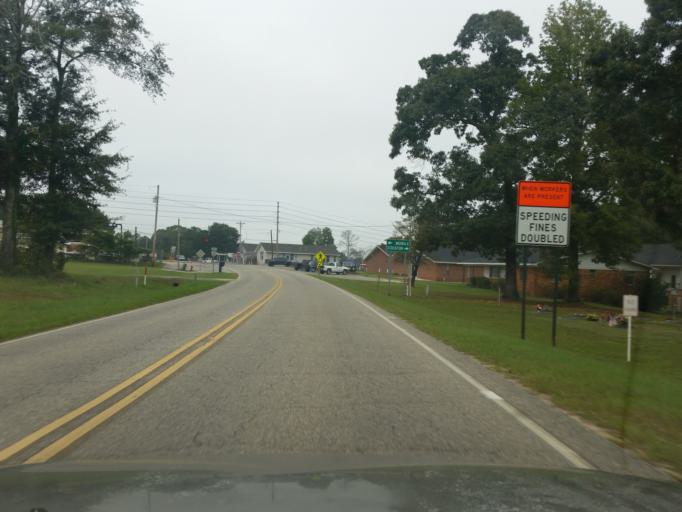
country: US
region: Alabama
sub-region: Baldwin County
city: Bay Minette
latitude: 30.8348
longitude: -87.8600
